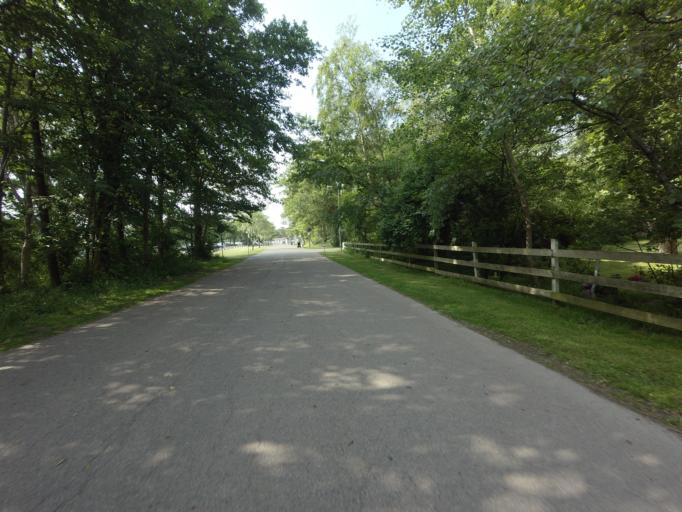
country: SE
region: Skane
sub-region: Angelholms Kommun
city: AEngelholm
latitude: 56.2555
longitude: 12.8341
